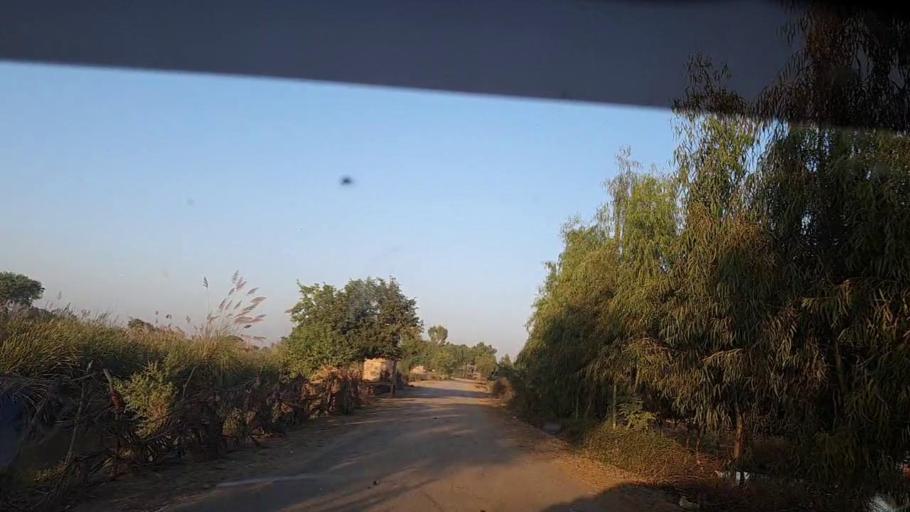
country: PK
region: Sindh
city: Ratodero
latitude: 27.9035
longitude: 68.2376
